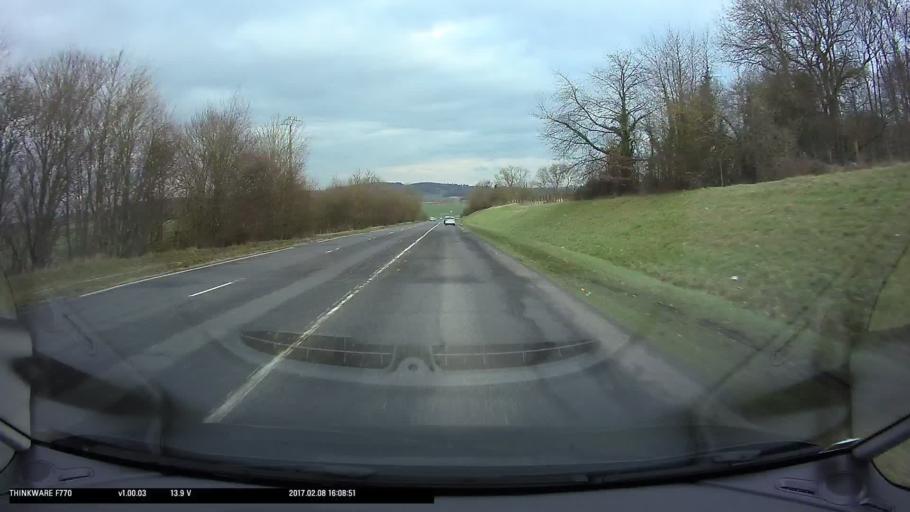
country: FR
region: Ile-de-France
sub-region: Departement du Val-d'Oise
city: Marines
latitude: 49.1230
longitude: 2.0072
